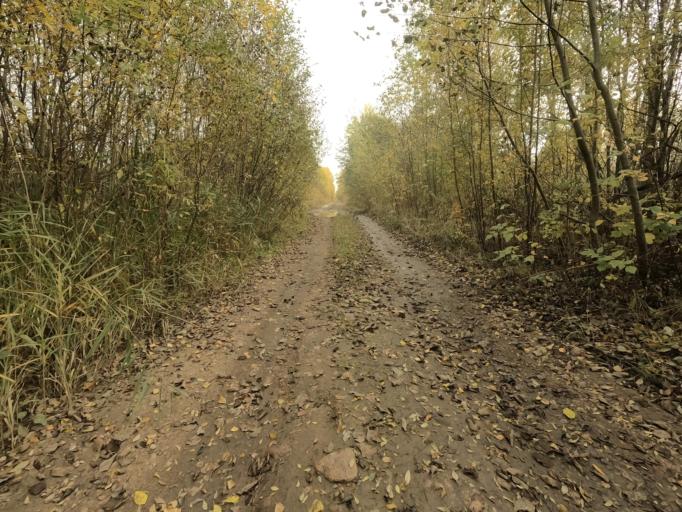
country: RU
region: Novgorod
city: Batetskiy
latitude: 58.8797
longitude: 30.7977
